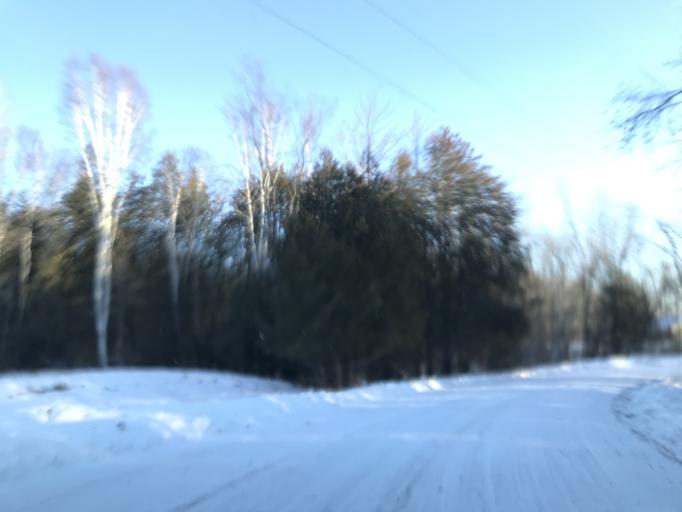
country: US
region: Michigan
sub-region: Menominee County
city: Menominee
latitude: 45.2937
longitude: -87.6951
